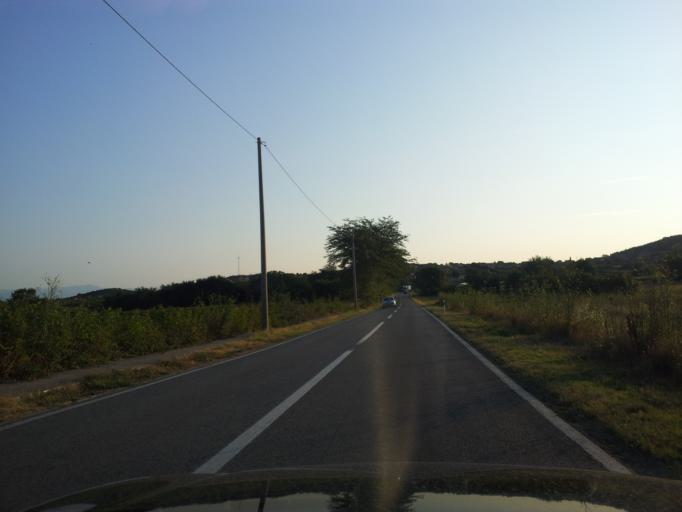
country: HR
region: Zadarska
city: Polaca
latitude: 44.0109
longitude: 15.5105
